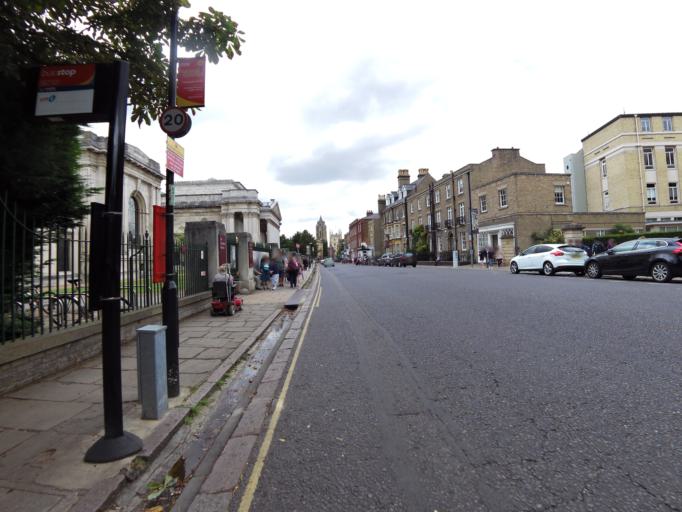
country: GB
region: England
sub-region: Cambridgeshire
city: Cambridge
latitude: 52.1996
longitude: 0.1209
